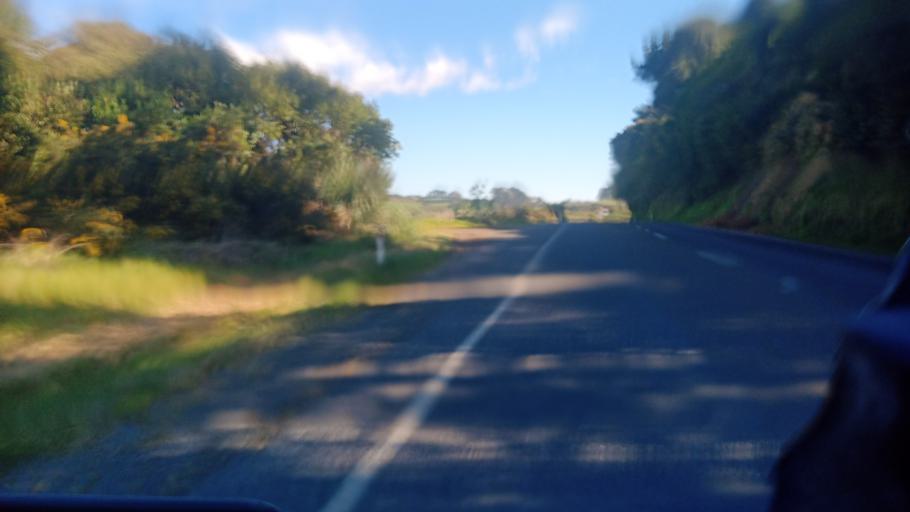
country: NZ
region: Bay of Plenty
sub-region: Opotiki District
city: Opotiki
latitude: -37.9907
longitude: 177.3453
